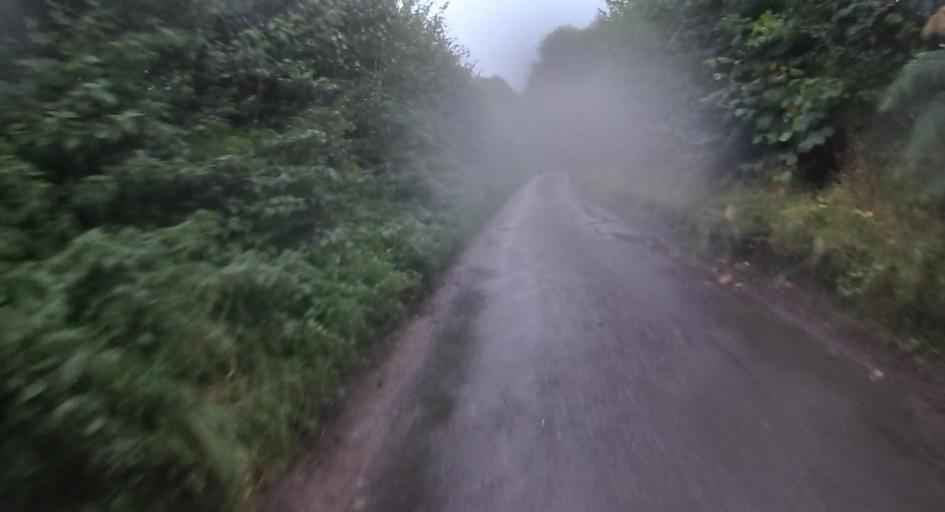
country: GB
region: England
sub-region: West Berkshire
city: Thatcham
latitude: 51.4065
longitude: -1.2112
